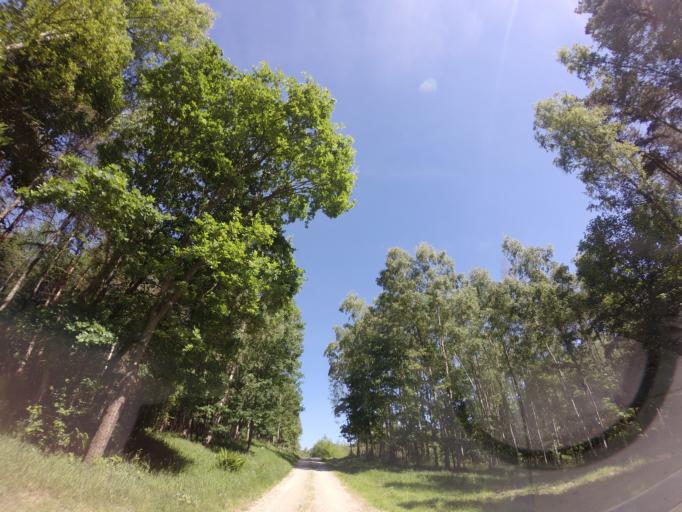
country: PL
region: West Pomeranian Voivodeship
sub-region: Powiat choszczenski
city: Recz
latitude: 53.3001
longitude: 15.5976
